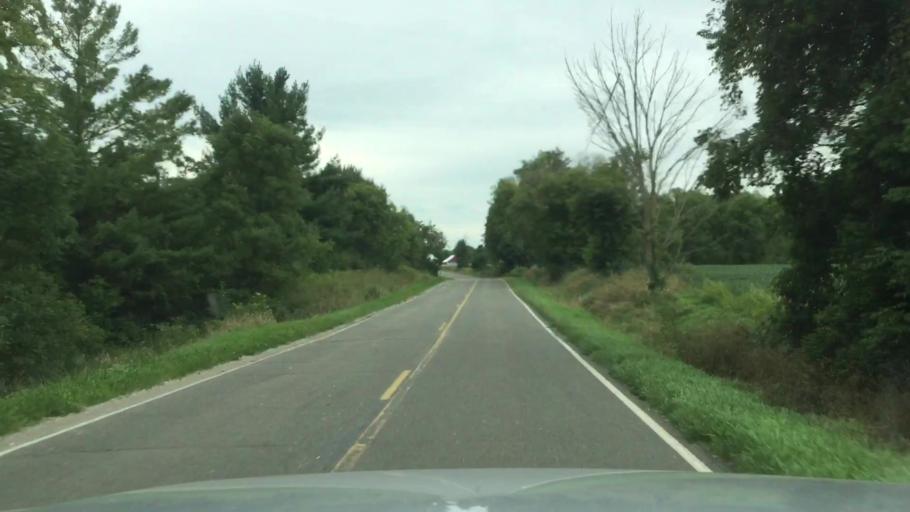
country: US
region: Michigan
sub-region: Shiawassee County
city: Durand
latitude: 42.8491
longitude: -84.0369
